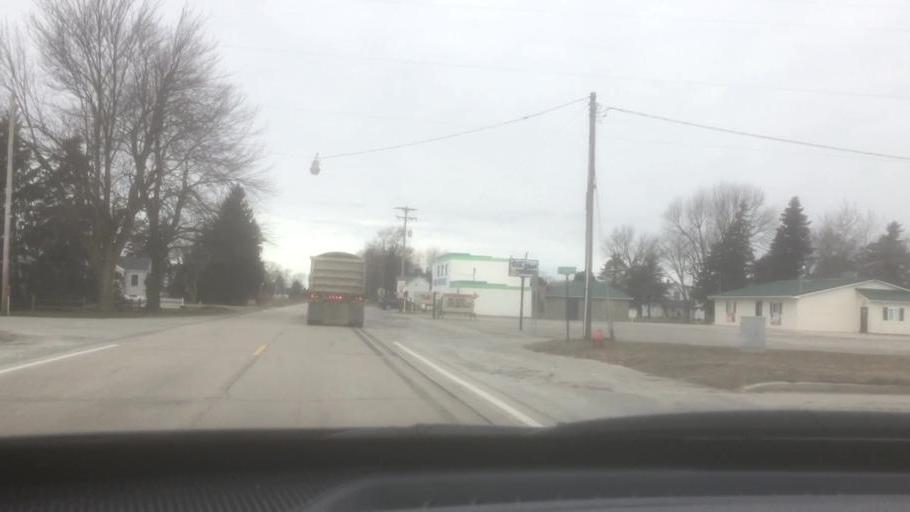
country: US
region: Michigan
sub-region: Tuscola County
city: Reese
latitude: 43.5220
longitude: -83.7780
